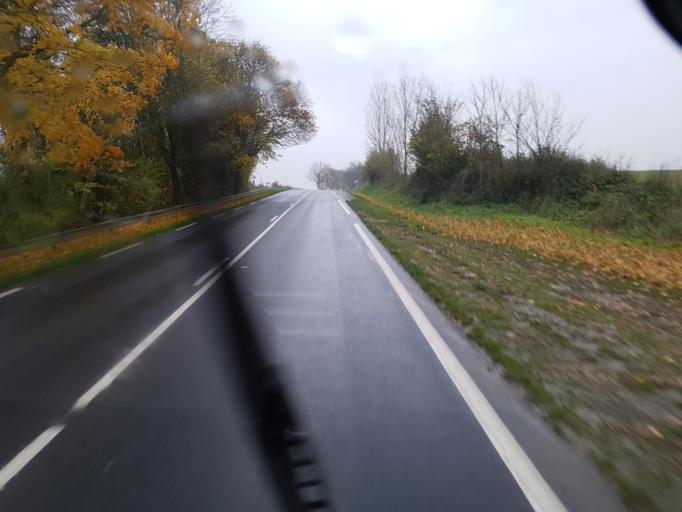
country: FR
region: Picardie
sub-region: Departement de l'Aisne
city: Saint-Quentin
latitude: 49.8744
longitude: 3.2696
